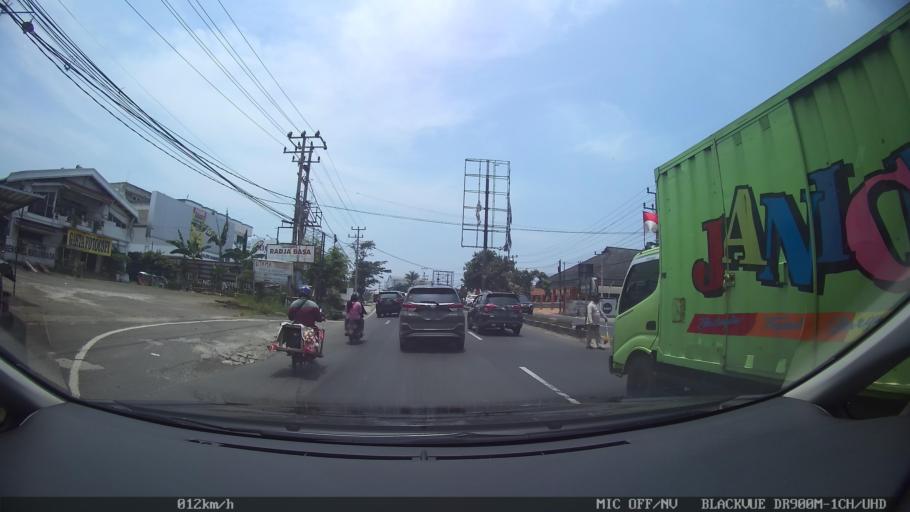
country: ID
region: Lampung
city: Kedaton
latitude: -5.3531
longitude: 105.2188
